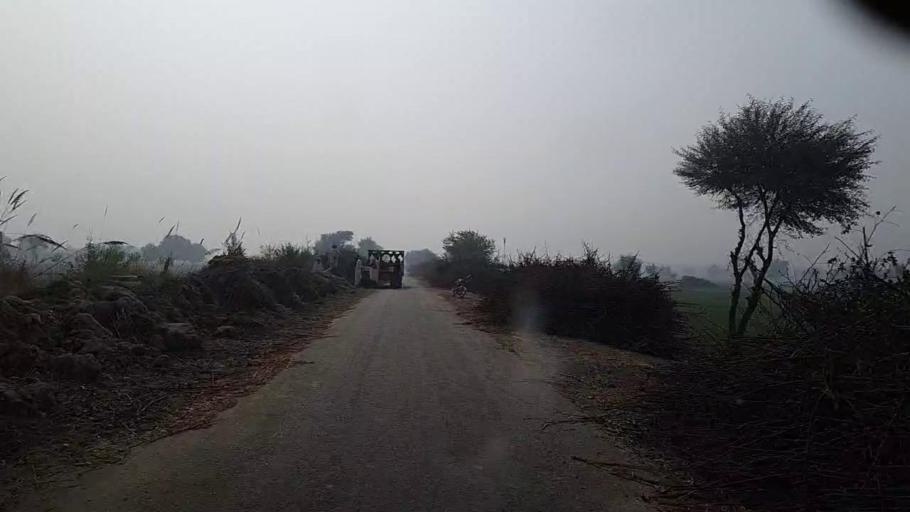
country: PK
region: Sindh
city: Kandiari
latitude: 26.9914
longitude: 68.6047
